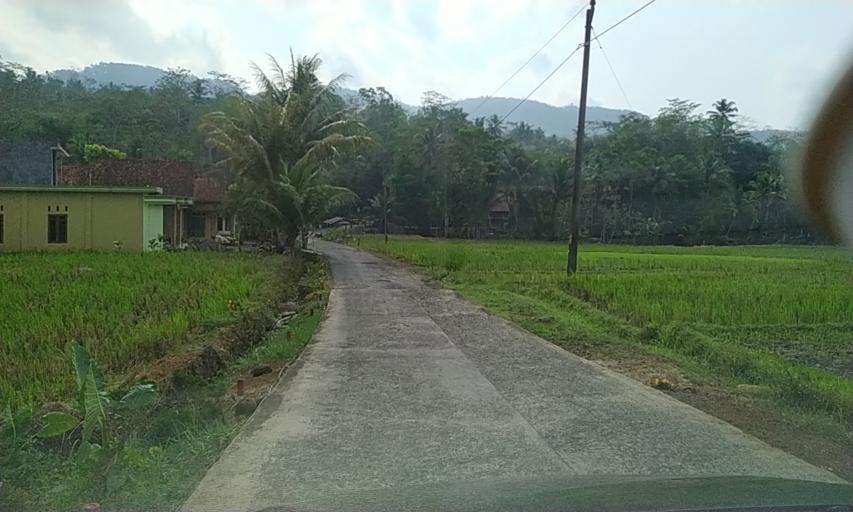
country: ID
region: Central Java
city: Dayeuhluhur
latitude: -7.2598
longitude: 108.6179
